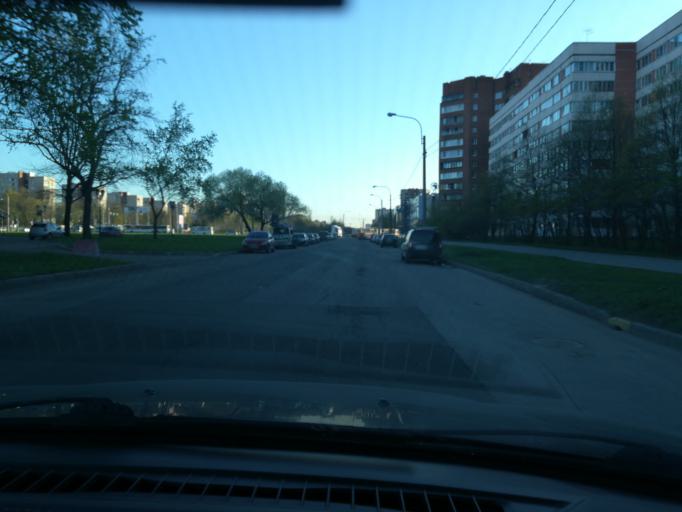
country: RU
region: St.-Petersburg
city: Avtovo
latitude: 59.8606
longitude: 30.2545
